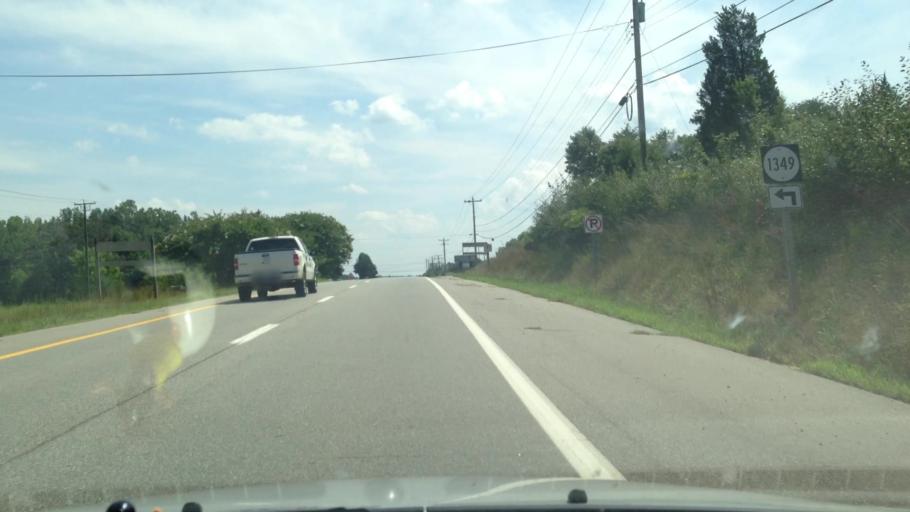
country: US
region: Virginia
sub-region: Henry County
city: Chatmoss
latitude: 36.6344
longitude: -79.8591
